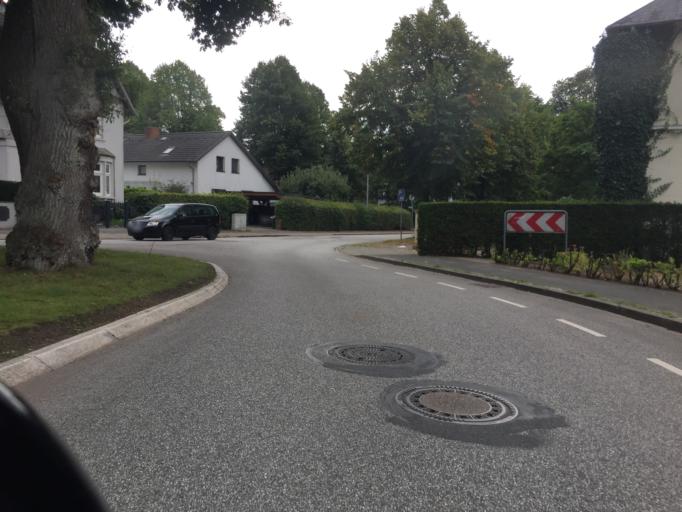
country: DE
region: Schleswig-Holstein
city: Itzehoe
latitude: 53.9356
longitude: 9.5082
